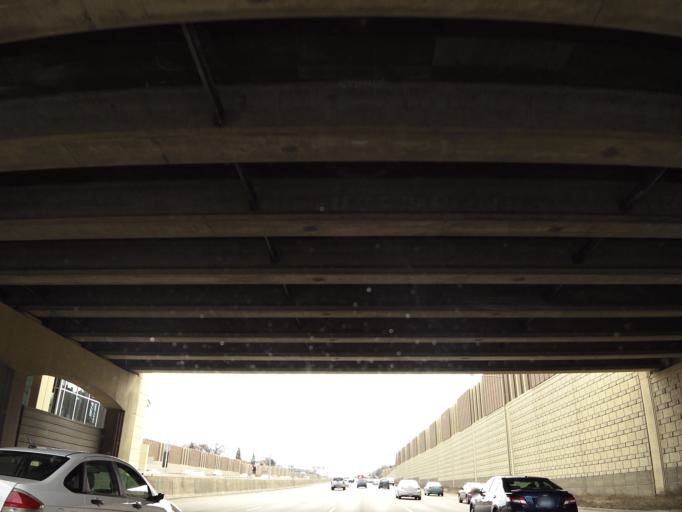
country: US
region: Minnesota
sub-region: Hennepin County
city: Richfield
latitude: 44.9198
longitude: -93.2751
